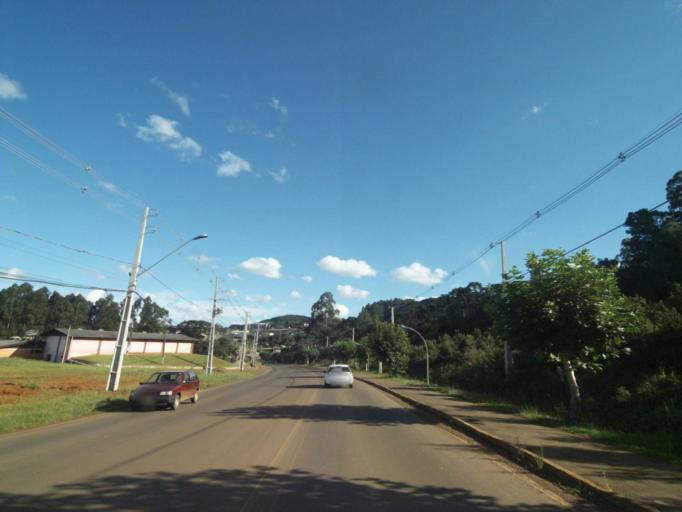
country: BR
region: Parana
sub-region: Uniao Da Vitoria
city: Uniao da Vitoria
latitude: -26.1570
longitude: -51.5417
